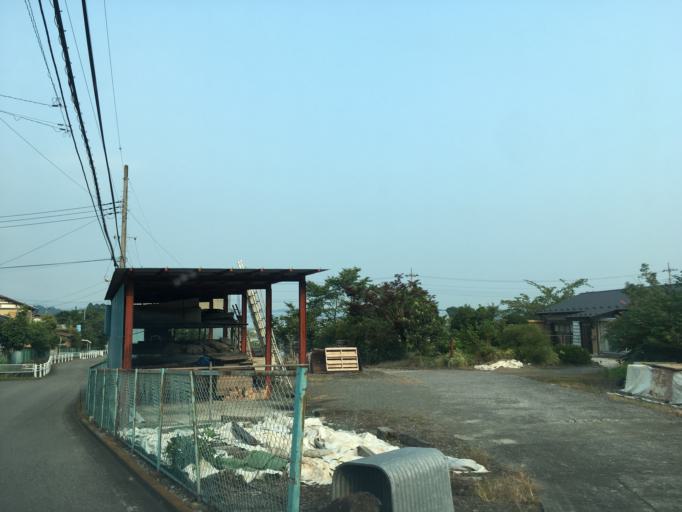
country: JP
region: Saitama
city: Chichibu
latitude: 35.9849
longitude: 139.1117
